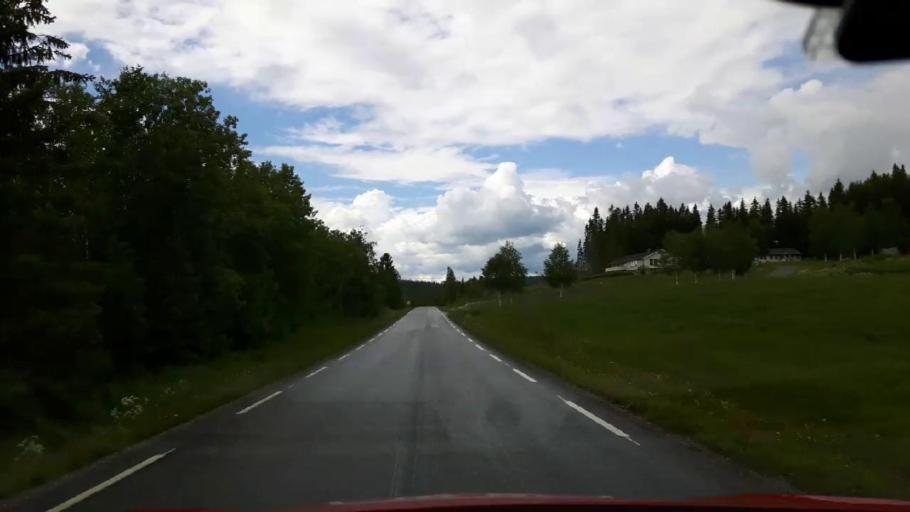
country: NO
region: Nord-Trondelag
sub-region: Lierne
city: Sandvika
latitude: 64.0955
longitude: 14.0396
